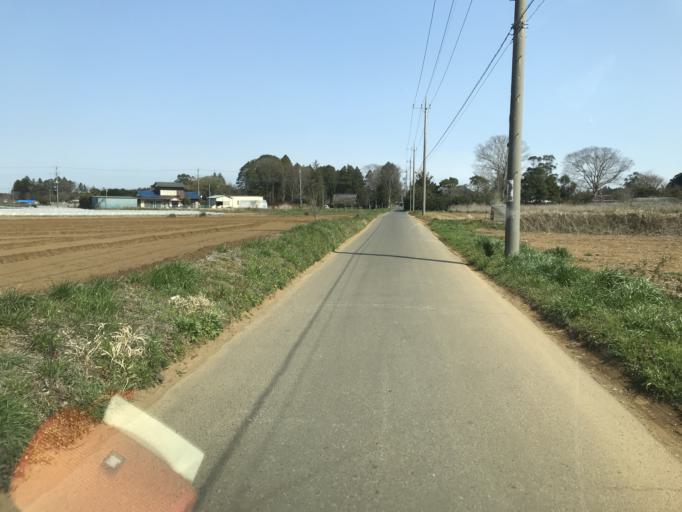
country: JP
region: Chiba
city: Sawara
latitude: 35.8357
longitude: 140.5226
